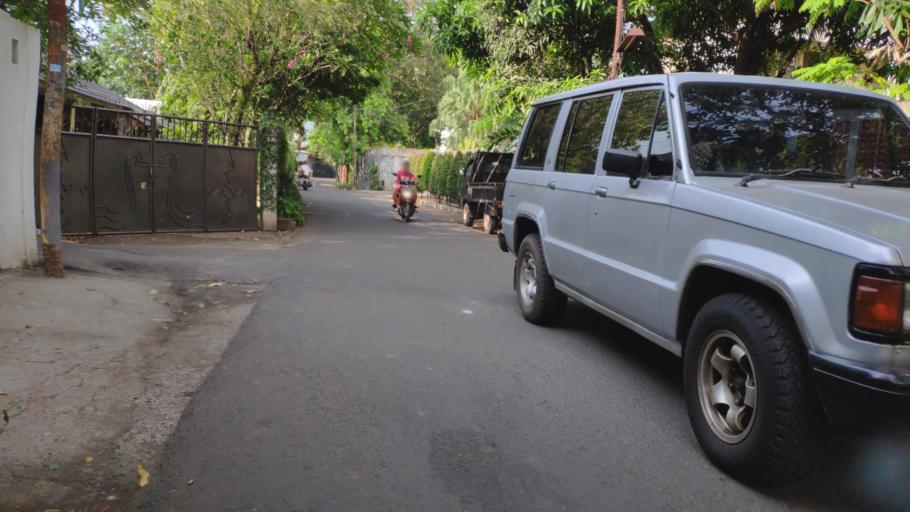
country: ID
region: West Java
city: Pamulang
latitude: -6.3012
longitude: 106.8020
